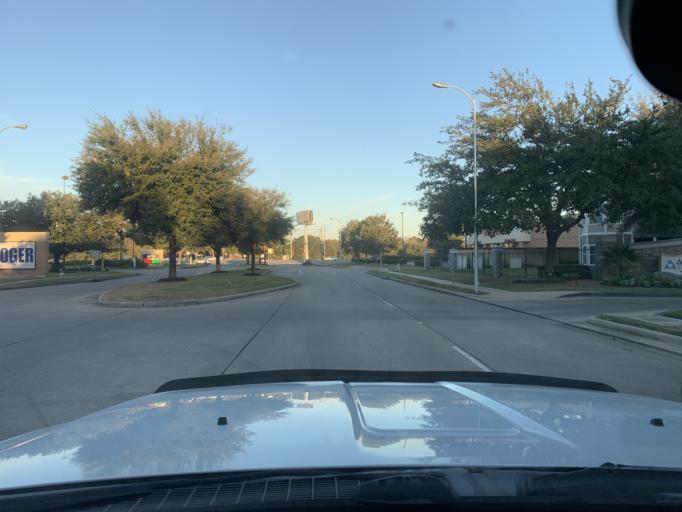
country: US
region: Texas
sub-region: Fort Bend County
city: Four Corners
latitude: 29.6491
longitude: -95.6493
